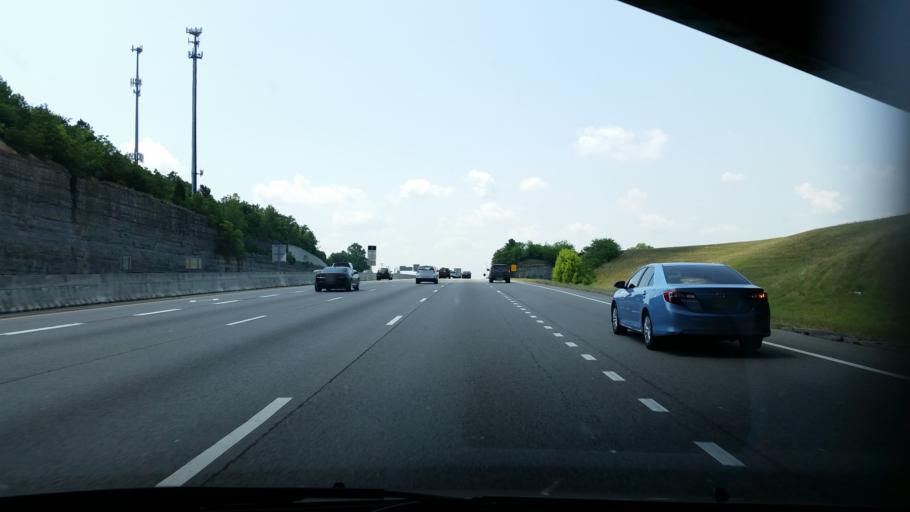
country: US
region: Tennessee
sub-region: Williamson County
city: Brentwood
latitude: 36.0388
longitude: -86.7829
